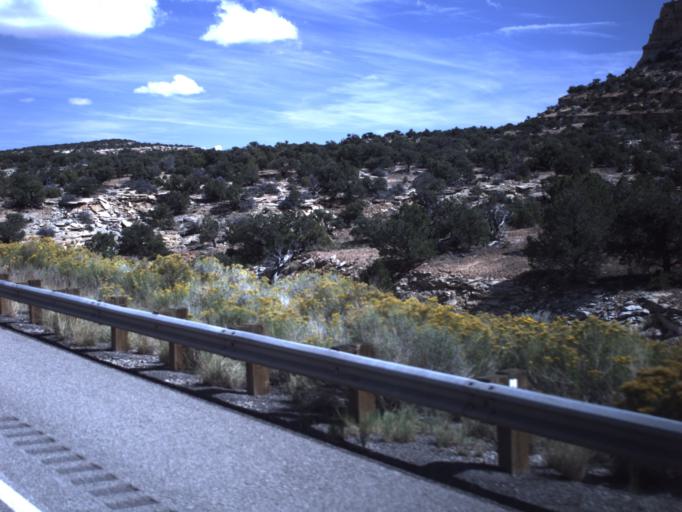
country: US
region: Utah
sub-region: Emery County
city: Ferron
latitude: 38.8521
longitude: -110.8796
